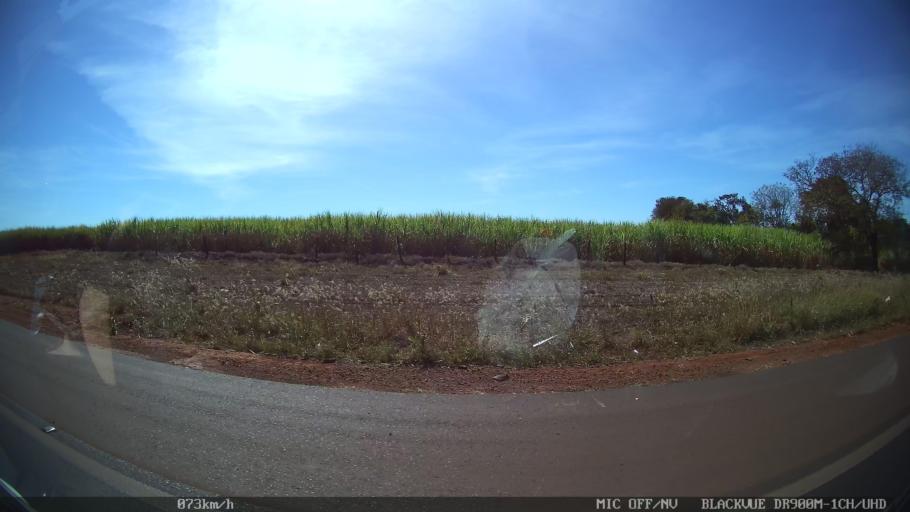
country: BR
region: Sao Paulo
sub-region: Ipua
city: Ipua
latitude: -20.5055
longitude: -47.9300
